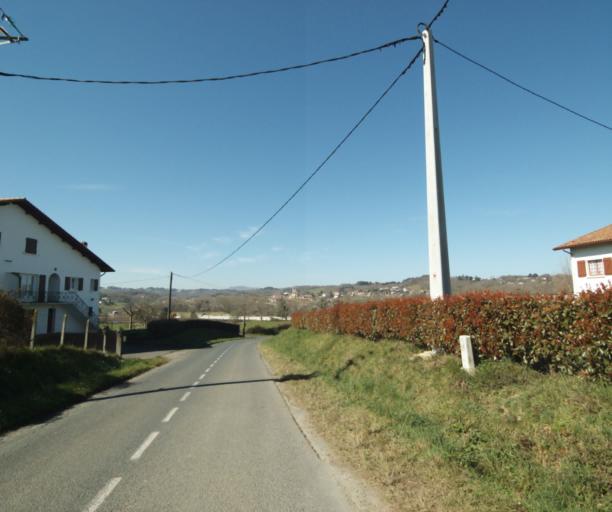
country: FR
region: Aquitaine
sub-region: Departement des Pyrenees-Atlantiques
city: Urrugne
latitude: 43.3624
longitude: -1.6880
